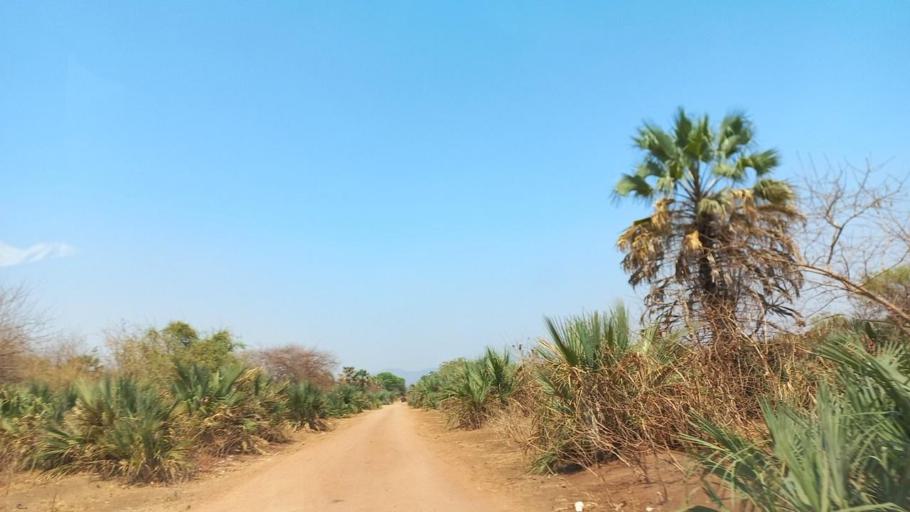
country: ZM
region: Lusaka
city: Luangwa
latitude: -15.1867
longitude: 30.2144
